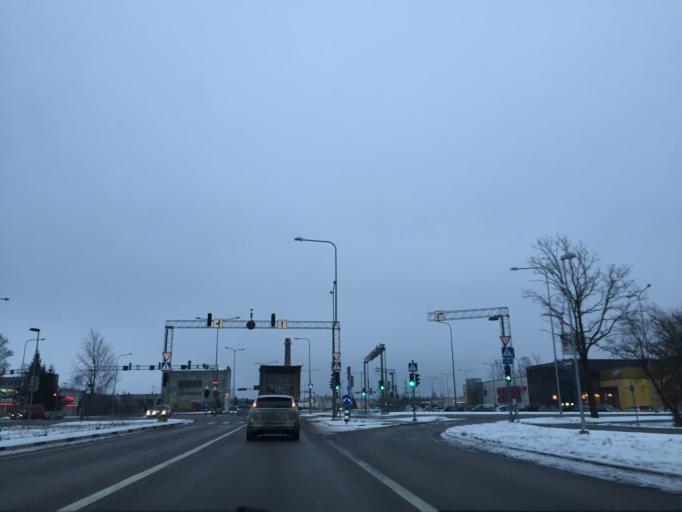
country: EE
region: Paernumaa
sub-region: Sauga vald
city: Sauga
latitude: 58.4090
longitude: 24.4924
